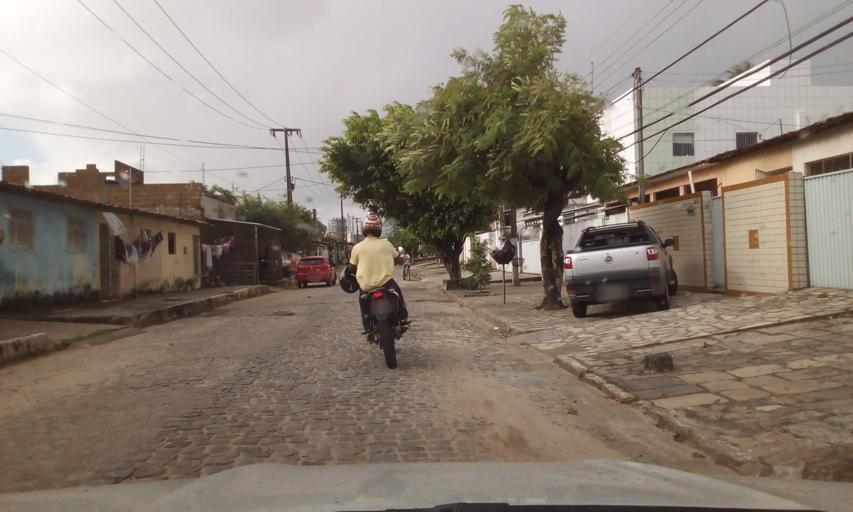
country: BR
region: Paraiba
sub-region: Joao Pessoa
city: Joao Pessoa
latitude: -7.1306
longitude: -34.8468
